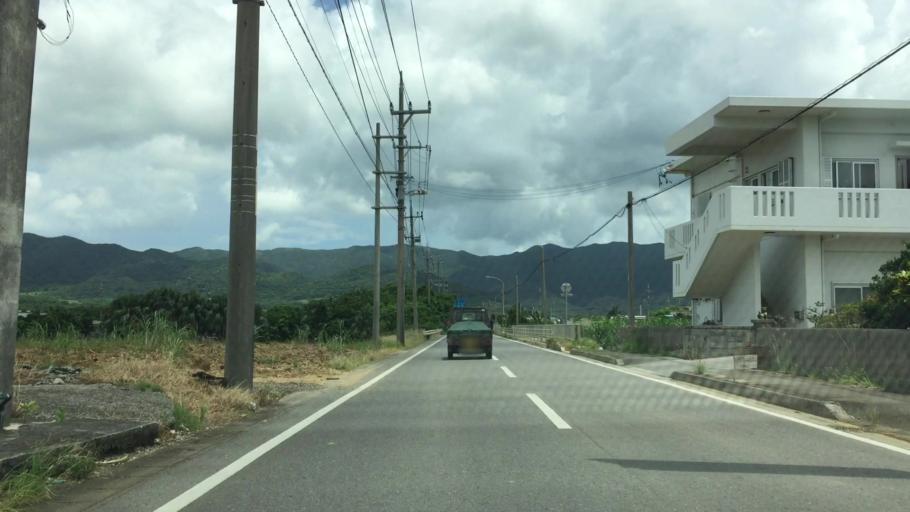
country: JP
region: Okinawa
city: Ishigaki
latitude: 24.3927
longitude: 124.1556
